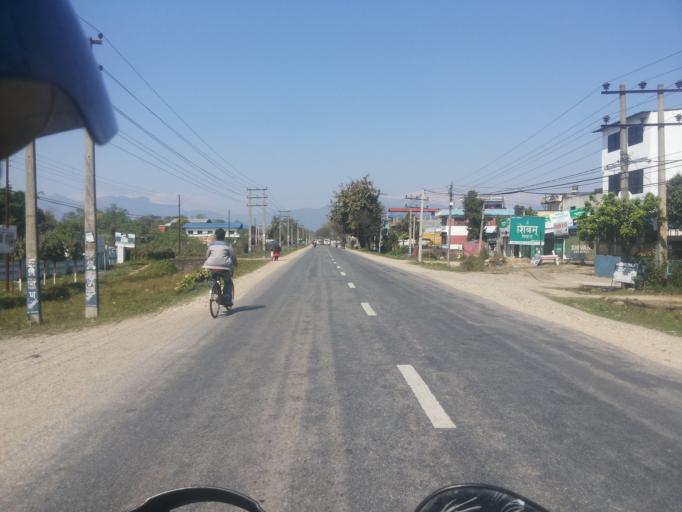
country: NP
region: Central Region
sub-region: Narayani Zone
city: Bharatpur
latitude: 27.6757
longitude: 84.4389
